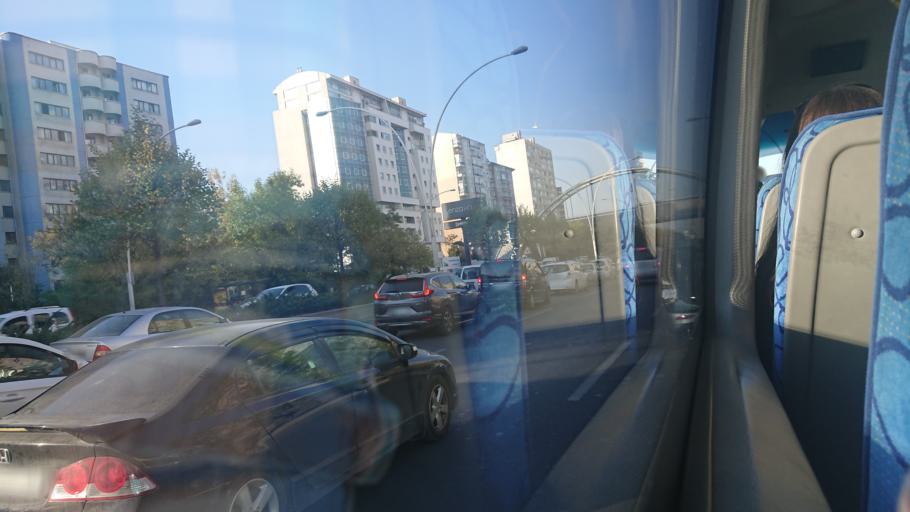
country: TR
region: Ankara
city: Ankara
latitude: 39.9277
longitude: 32.8163
